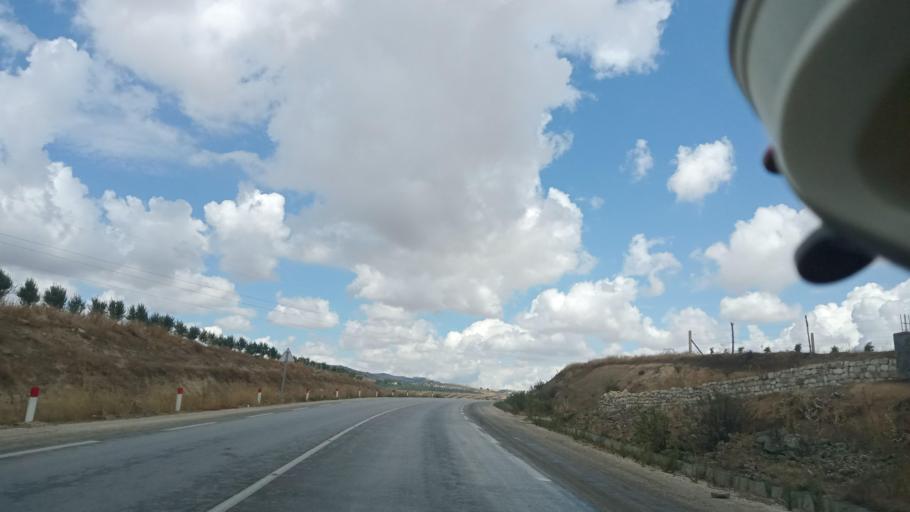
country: TN
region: Silyanah
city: Al Karib
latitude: 36.3008
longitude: 9.0813
